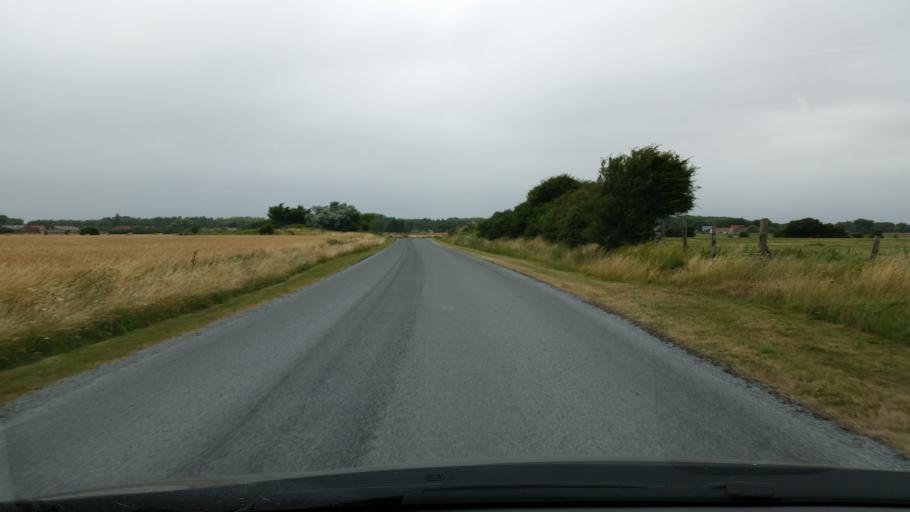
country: FR
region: Nord-Pas-de-Calais
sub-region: Departement du Pas-de-Calais
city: Marck
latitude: 50.9607
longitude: 1.9397
